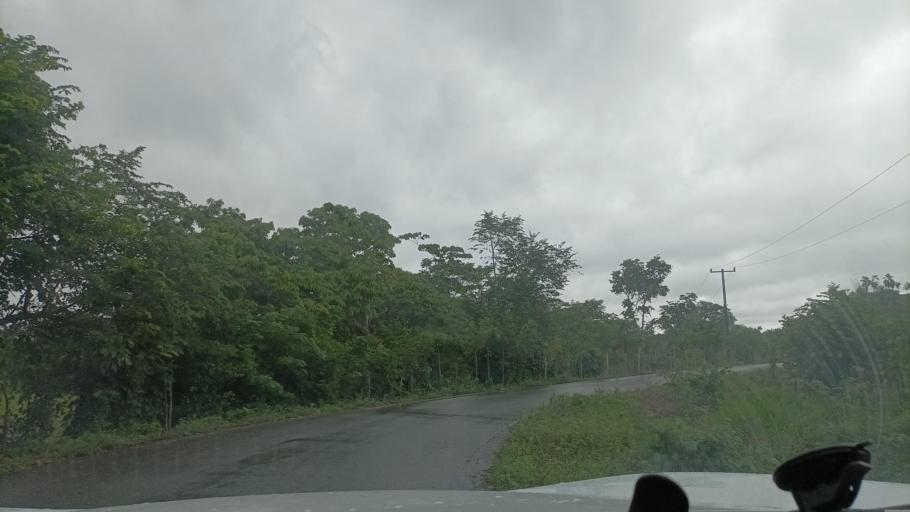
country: MX
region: Veracruz
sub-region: Moloacan
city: Cuichapa
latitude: 17.7566
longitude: -94.3948
